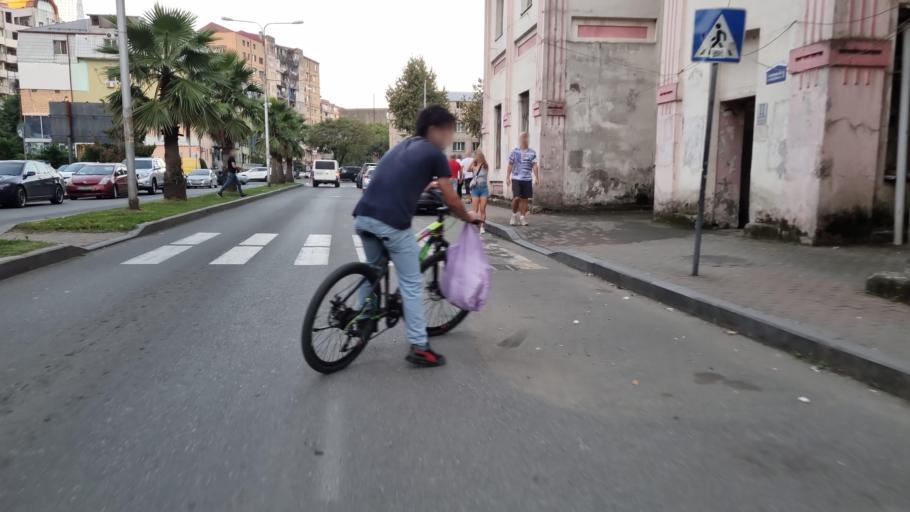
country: GE
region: Ajaria
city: Batumi
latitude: 41.6419
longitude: 41.6193
